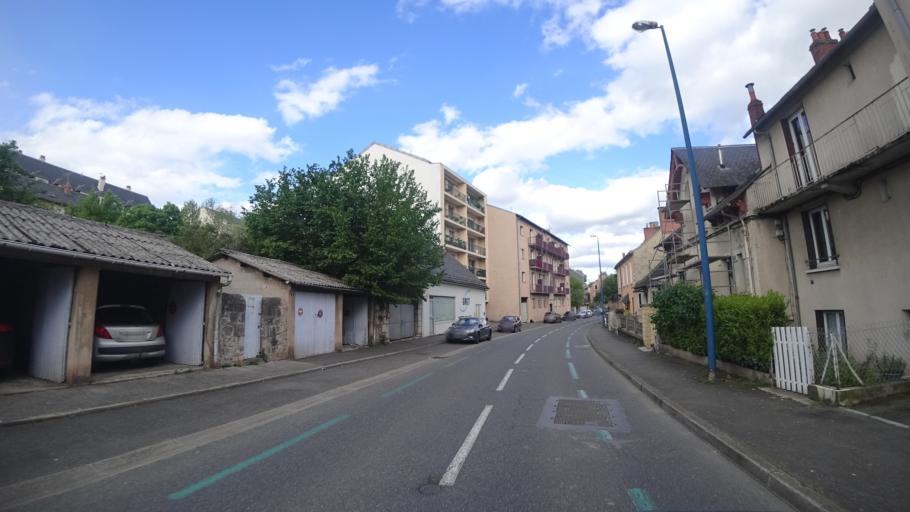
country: FR
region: Midi-Pyrenees
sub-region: Departement de l'Aveyron
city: Rodez
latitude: 44.3568
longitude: 2.5828
